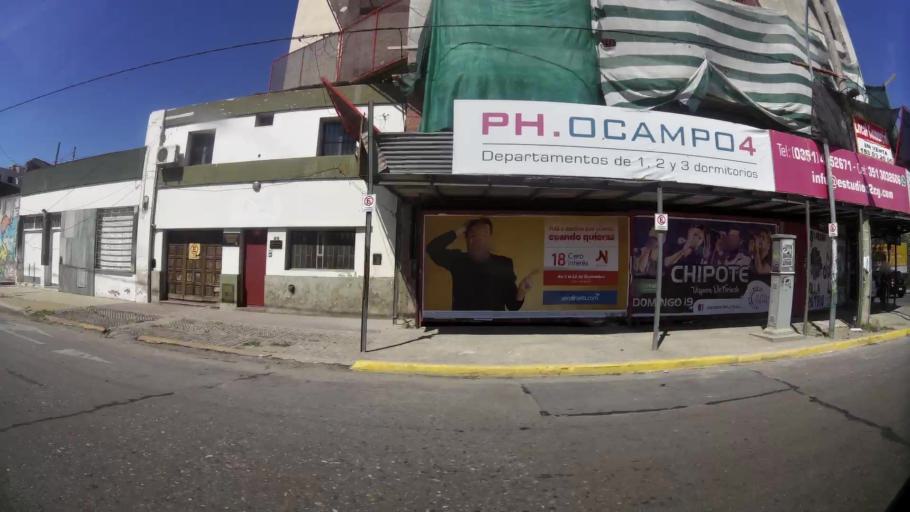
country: AR
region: Cordoba
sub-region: Departamento de Capital
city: Cordoba
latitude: -31.4177
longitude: -64.1724
